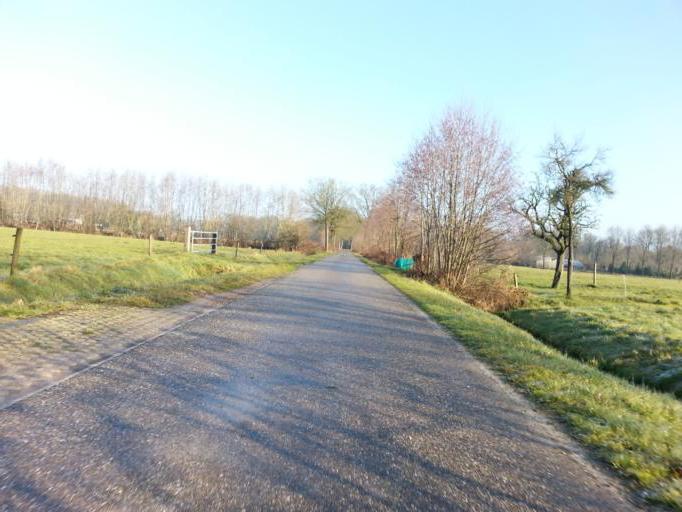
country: NL
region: Utrecht
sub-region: Gemeente Woudenberg
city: Woudenberg
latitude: 52.0992
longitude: 5.4099
